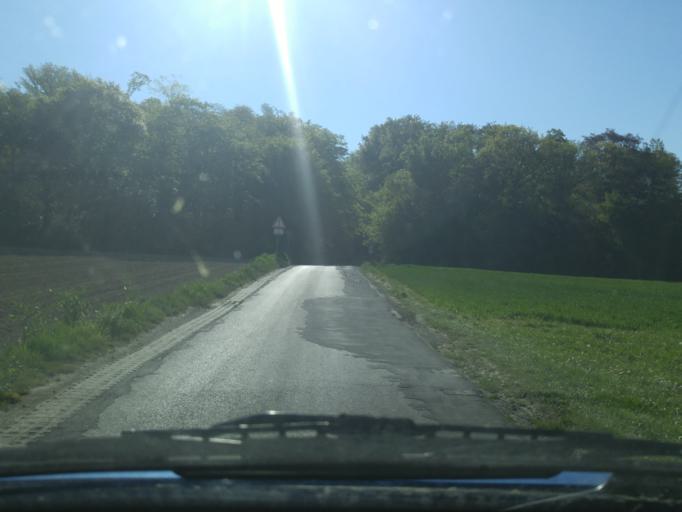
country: DE
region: Hesse
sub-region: Regierungsbezirk Darmstadt
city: Bad Nauheim
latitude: 50.3650
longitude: 8.7168
